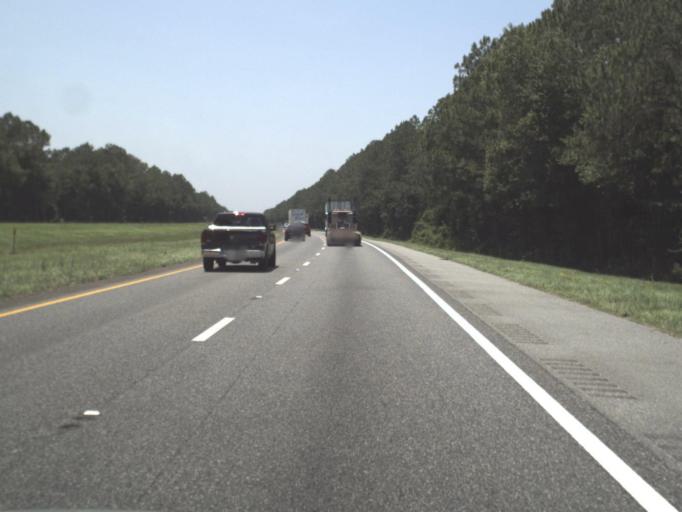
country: US
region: Florida
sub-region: Baker County
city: Macclenny
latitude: 30.2542
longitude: -82.3332
